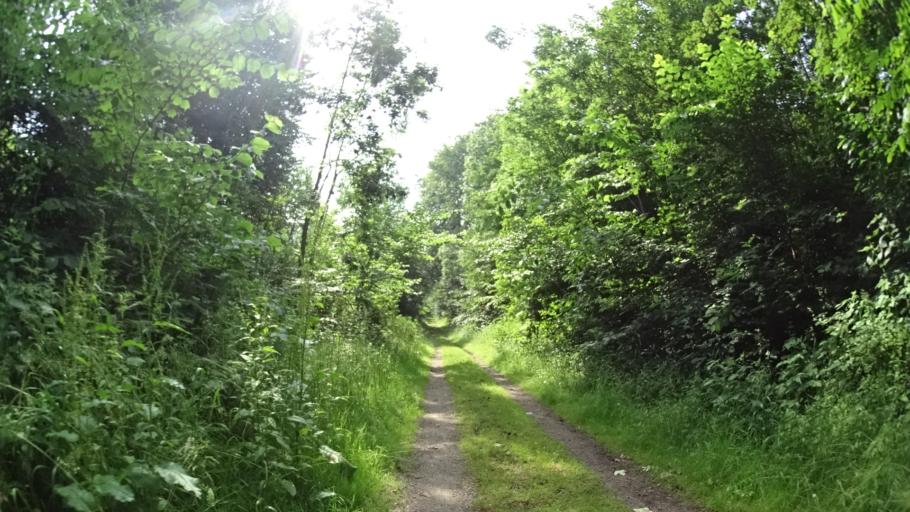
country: DK
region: Central Jutland
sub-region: Arhus Kommune
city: Stavtrup
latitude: 56.1401
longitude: 10.0917
